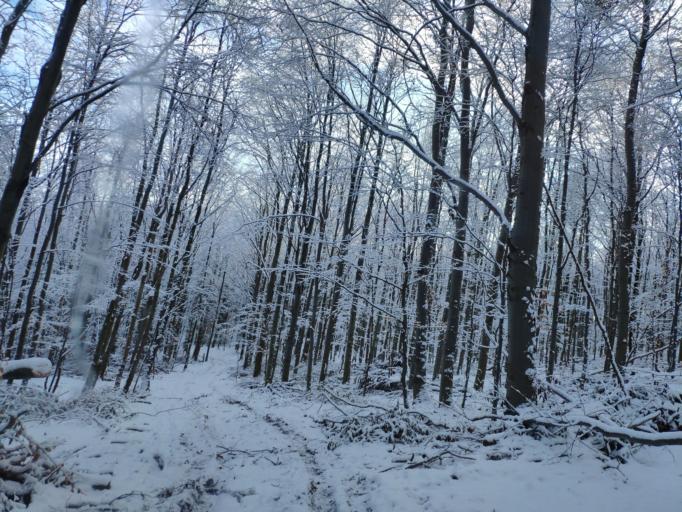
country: SK
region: Kosicky
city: Moldava nad Bodvou
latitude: 48.7477
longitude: 21.0839
